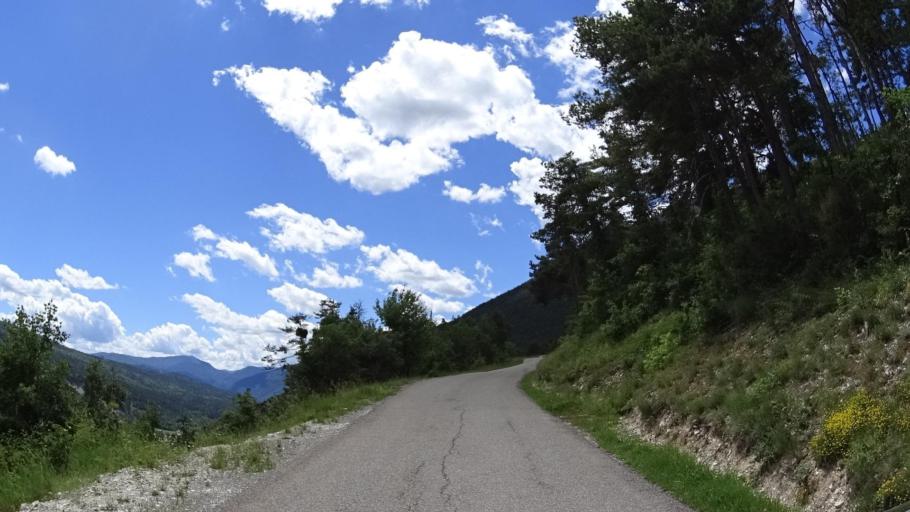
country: FR
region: Provence-Alpes-Cote d'Azur
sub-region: Departement des Alpes-de-Haute-Provence
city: Annot
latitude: 44.0145
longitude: 6.6293
